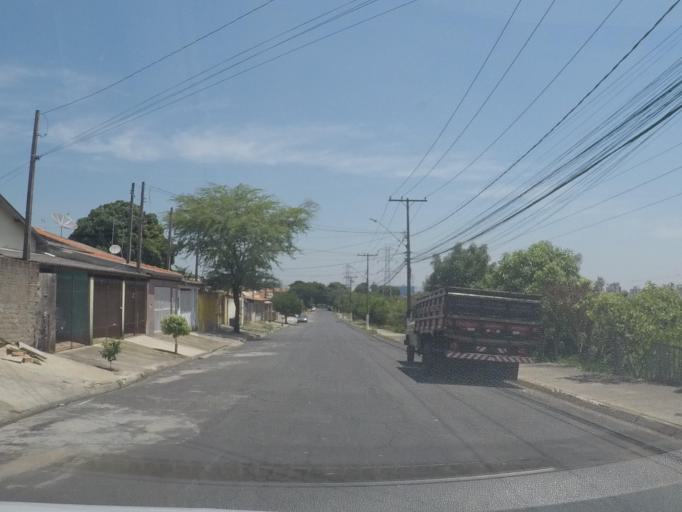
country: BR
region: Sao Paulo
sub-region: Hortolandia
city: Hortolandia
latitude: -22.8547
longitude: -47.1950
